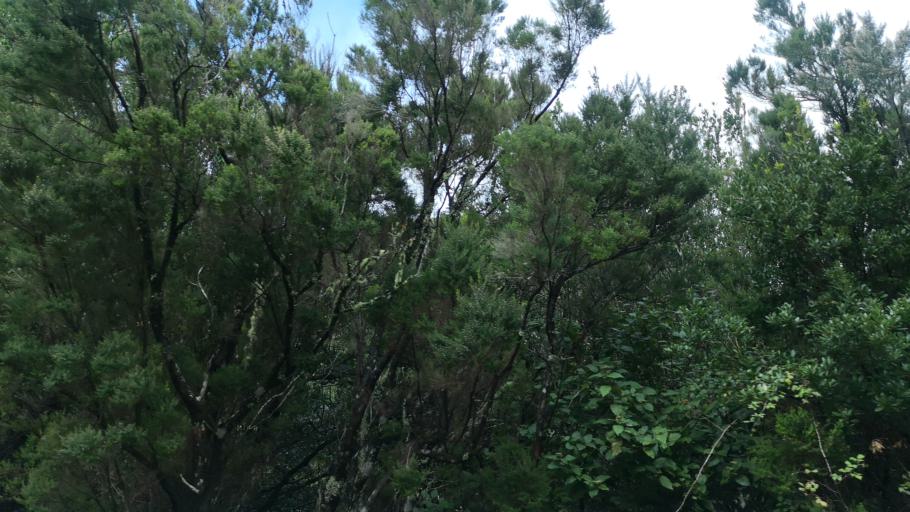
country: ES
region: Canary Islands
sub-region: Provincia de Santa Cruz de Tenerife
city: Vallehermosa
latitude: 28.1636
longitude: -17.2963
